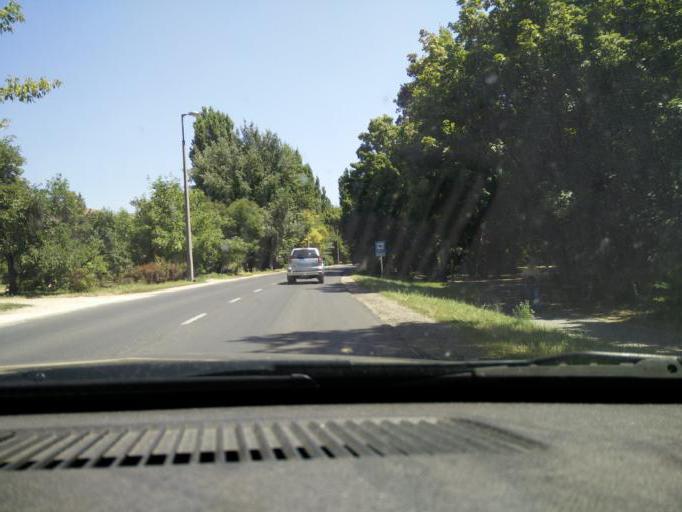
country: HU
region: Komarom-Esztergom
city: Tata
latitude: 47.6447
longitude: 18.3365
